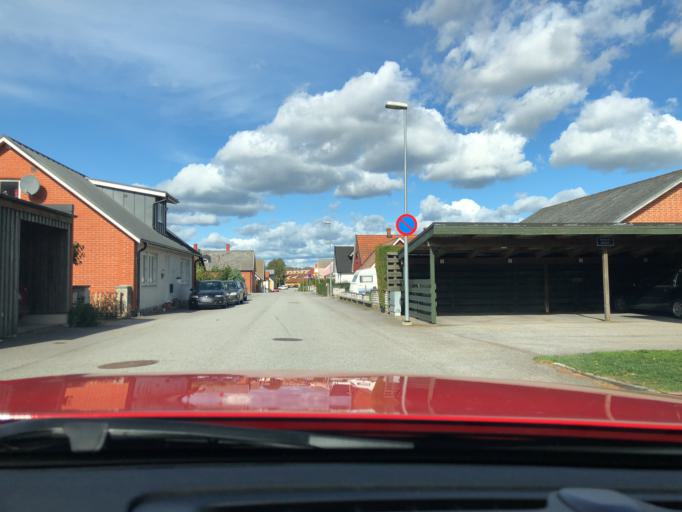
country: SE
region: Skane
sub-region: Sjobo Kommun
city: Sjoebo
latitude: 55.6344
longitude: 13.7054
